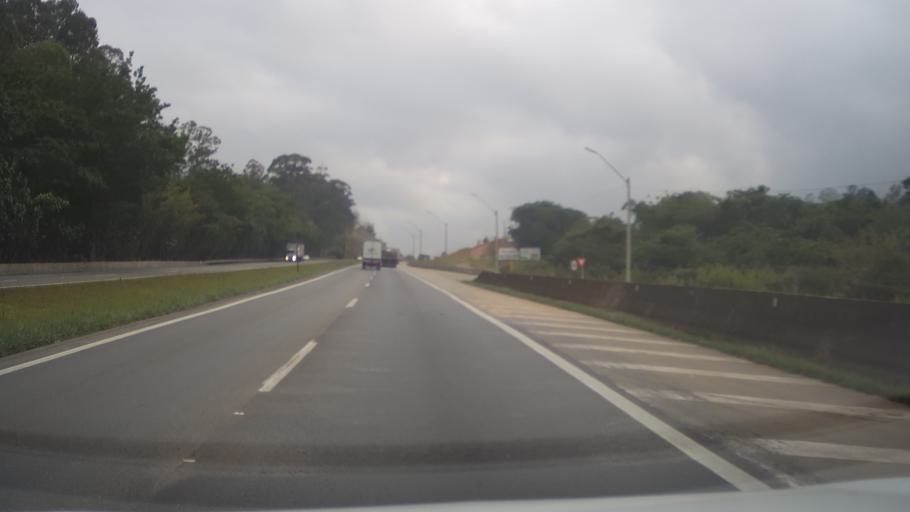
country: BR
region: Minas Gerais
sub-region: Extrema
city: Extrema
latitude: -22.8825
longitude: -46.3866
